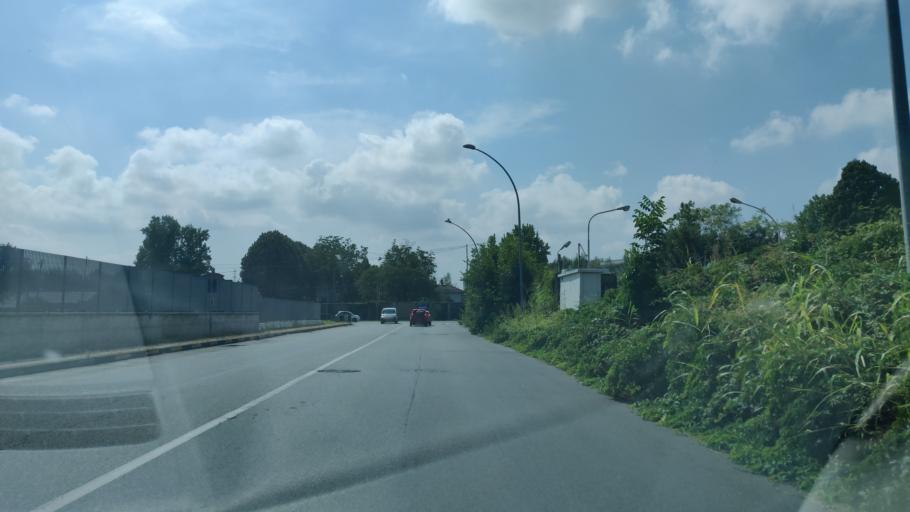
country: IT
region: Piedmont
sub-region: Provincia di Torino
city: Savonera
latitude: 45.0996
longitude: 7.6087
